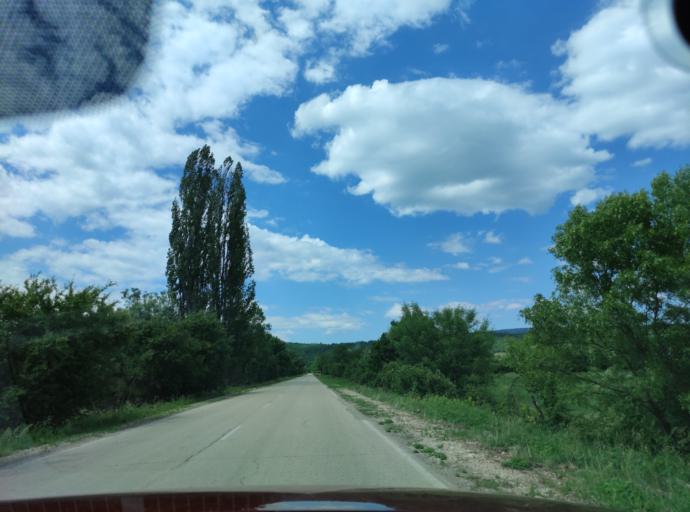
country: BG
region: Montana
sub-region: Obshtina Montana
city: Montana
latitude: 43.3956
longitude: 23.0736
